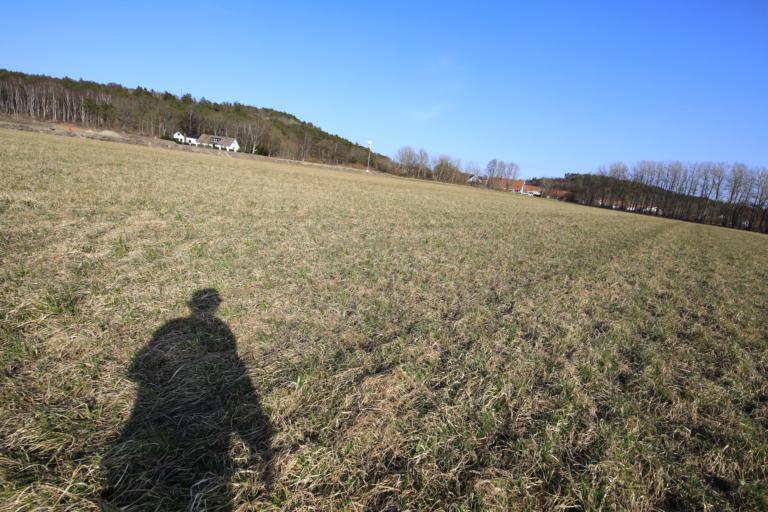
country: SE
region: Halland
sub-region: Varbergs Kommun
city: Varberg
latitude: 57.1419
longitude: 12.2794
